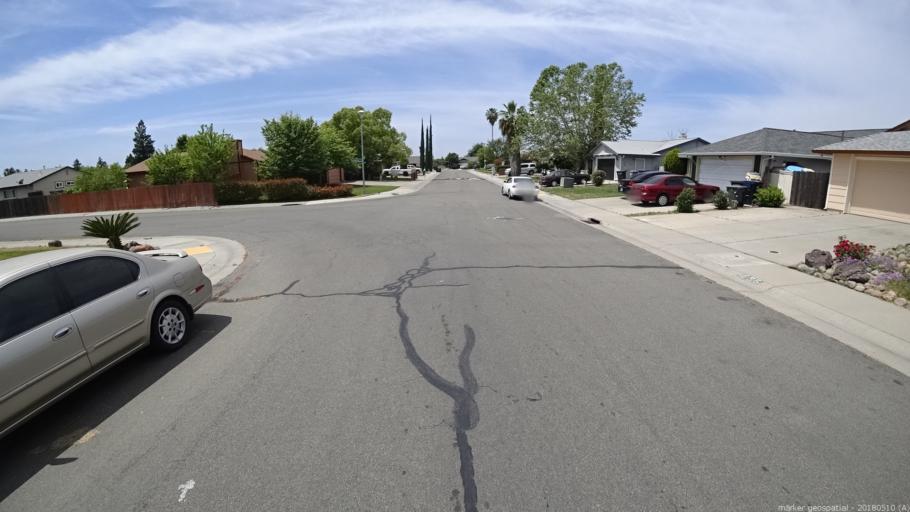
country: US
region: California
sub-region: Sacramento County
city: Rio Linda
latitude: 38.6527
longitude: -121.4527
